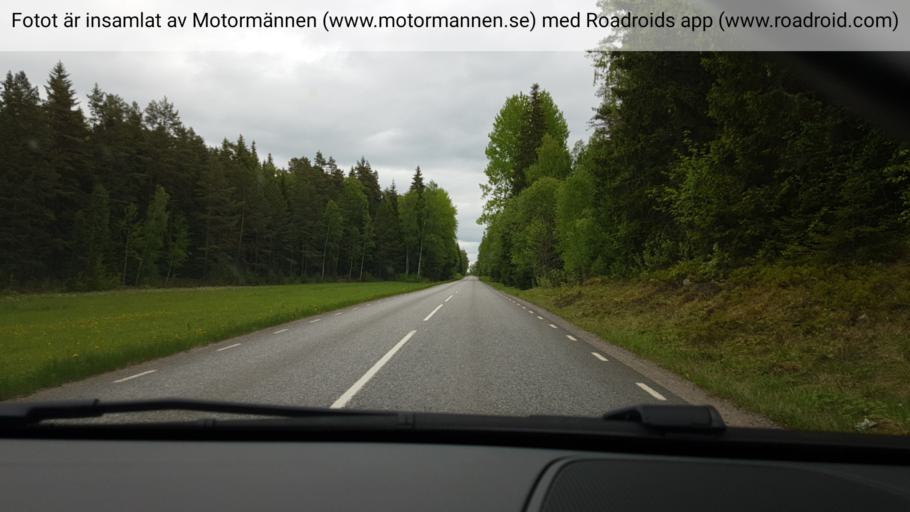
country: SE
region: Uppsala
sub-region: Heby Kommun
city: Tarnsjo
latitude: 60.0858
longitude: 17.0677
